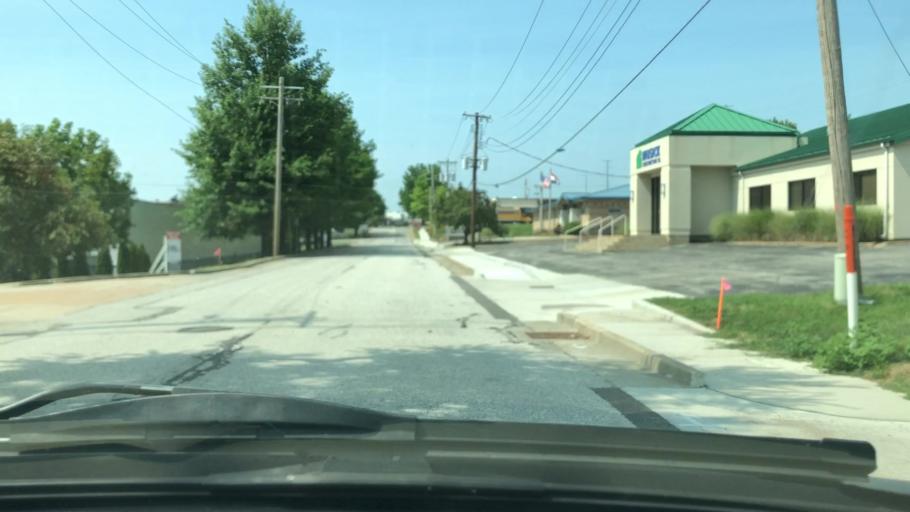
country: US
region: Missouri
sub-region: Saint Louis County
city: Brentwood
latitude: 38.6200
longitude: -90.3364
